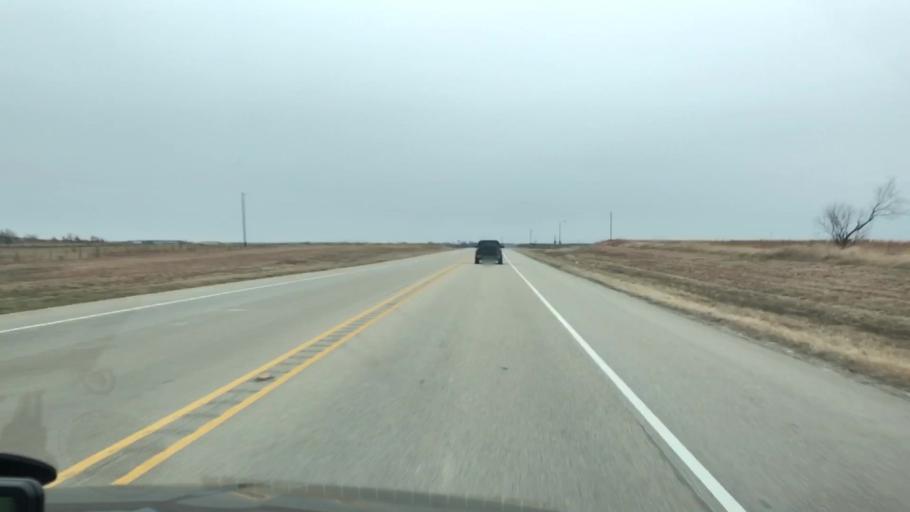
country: US
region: Texas
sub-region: Hamilton County
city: Hamilton
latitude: 31.6278
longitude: -98.1539
